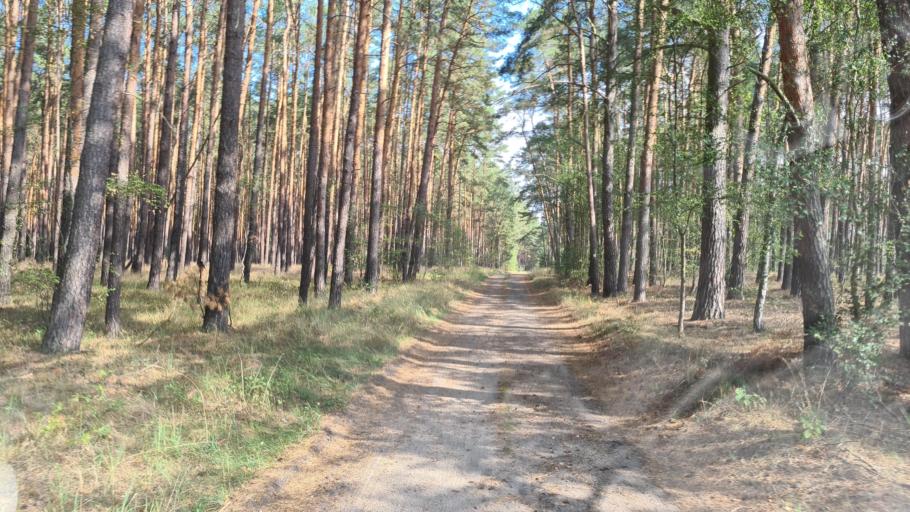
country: DE
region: Brandenburg
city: Belzig
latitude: 52.1568
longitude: 12.6529
